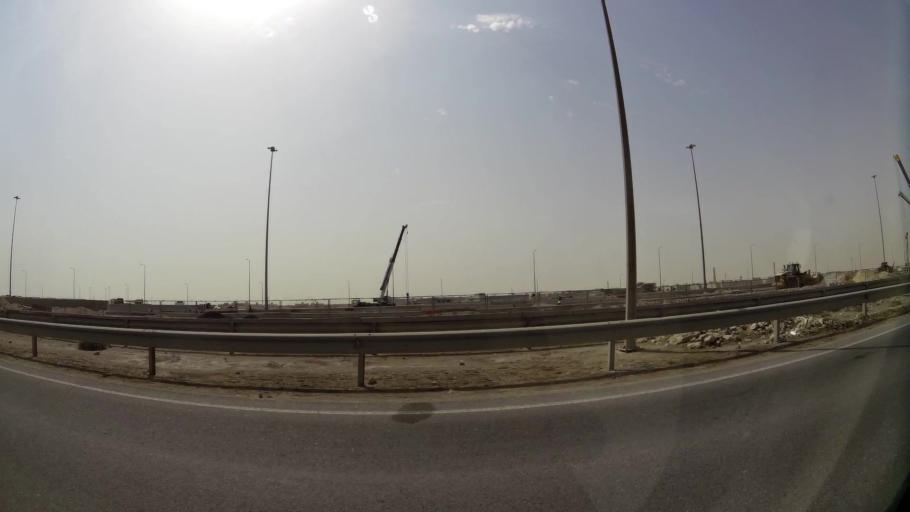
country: QA
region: Al Wakrah
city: Al Wukayr
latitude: 25.2003
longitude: 51.4718
